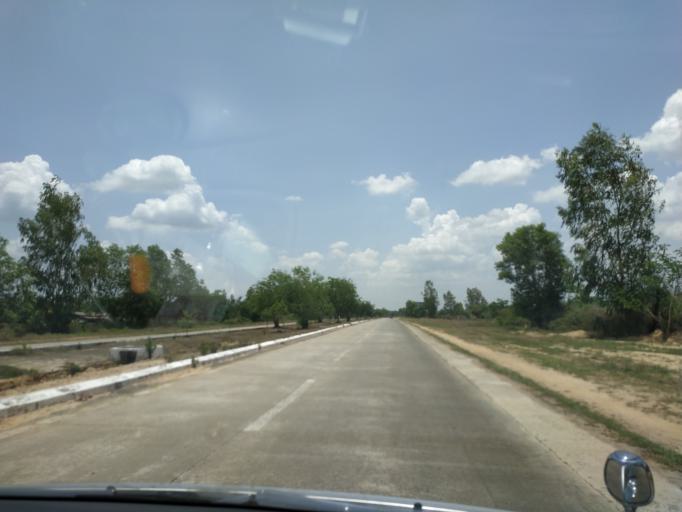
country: MM
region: Bago
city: Bago
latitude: 17.4626
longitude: 96.4348
